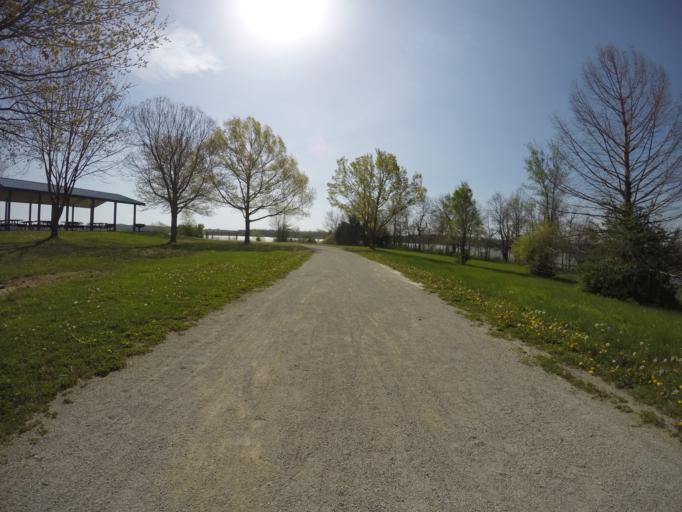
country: US
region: Missouri
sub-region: Jackson County
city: Grandview
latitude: 38.9074
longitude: -94.4788
